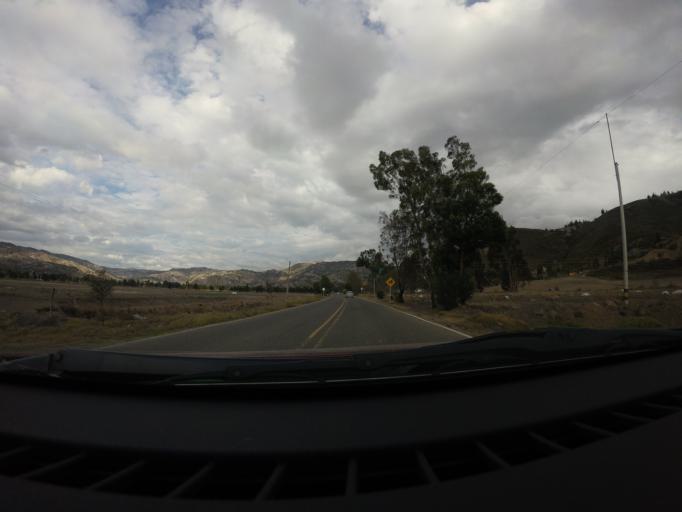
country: CO
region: Boyaca
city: Cucaita
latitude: 5.5411
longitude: -73.4727
